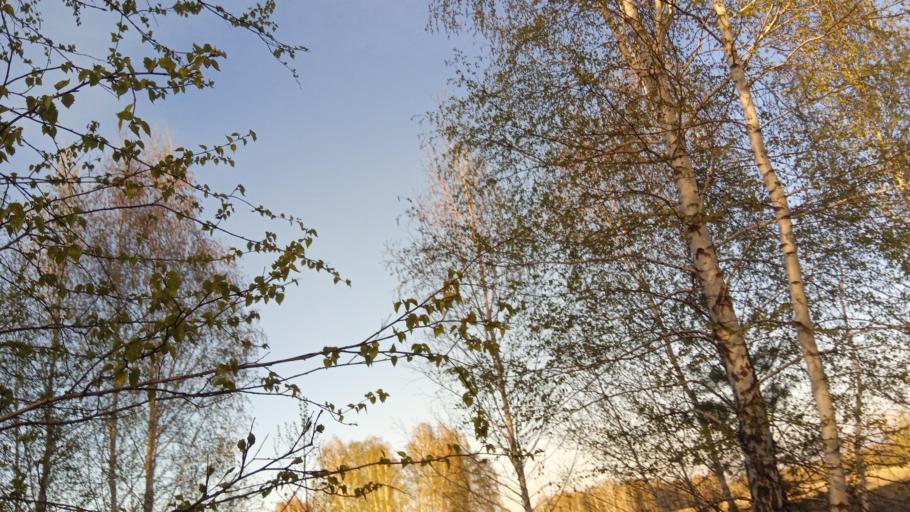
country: RU
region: Chelyabinsk
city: Timiryazevskiy
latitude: 54.9937
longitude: 60.8682
